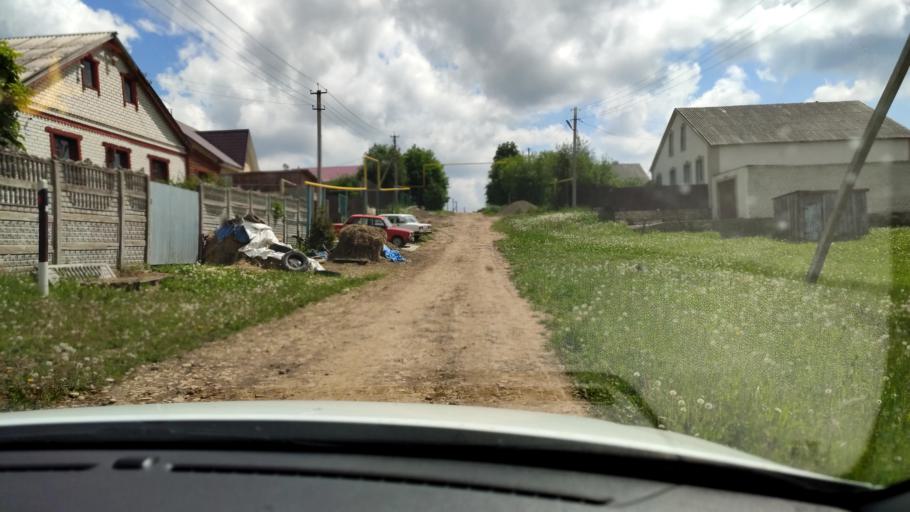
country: RU
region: Tatarstan
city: Vysokaya Gora
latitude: 56.0027
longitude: 49.3015
